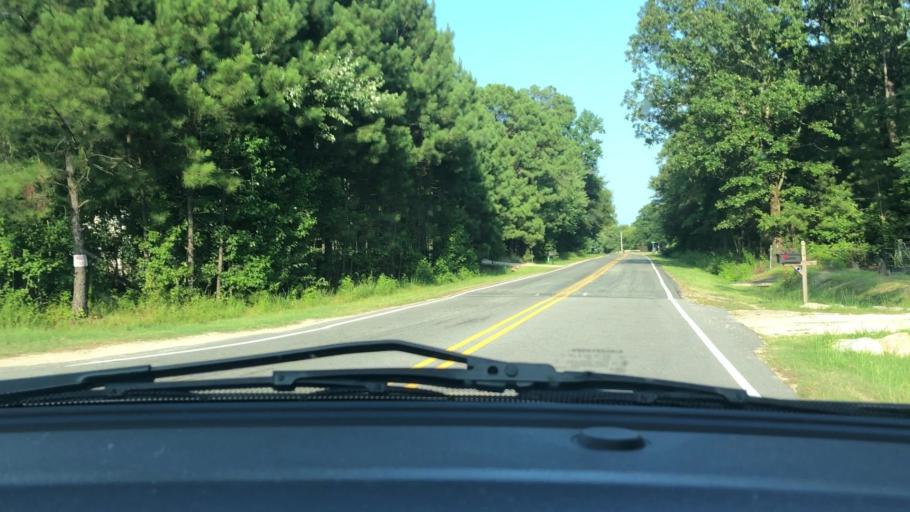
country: US
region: North Carolina
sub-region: Lee County
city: Broadway
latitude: 35.3279
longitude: -79.0598
